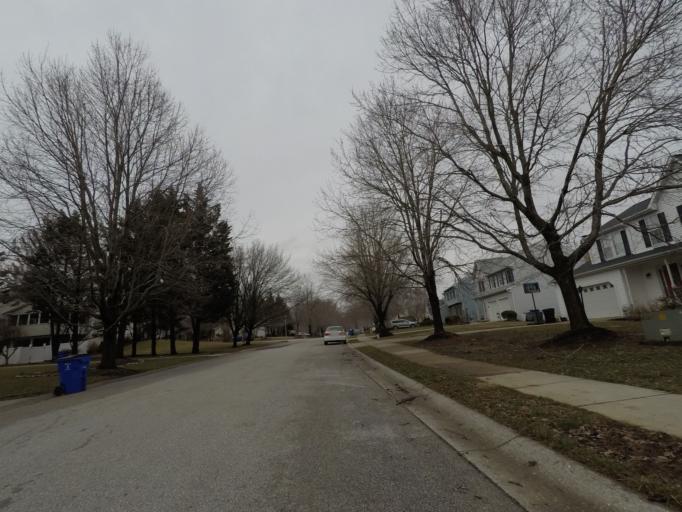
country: US
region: Maryland
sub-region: Howard County
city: Ilchester
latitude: 39.2196
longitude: -76.7821
